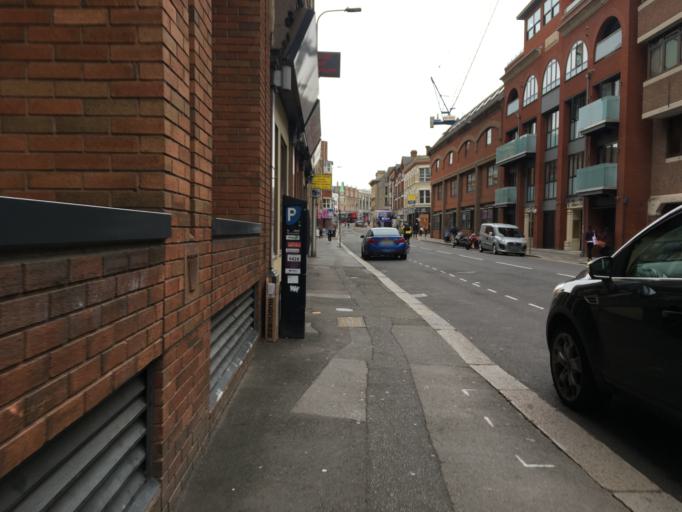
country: GB
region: England
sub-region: Reading
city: Reading
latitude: 51.4548
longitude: -0.9668
